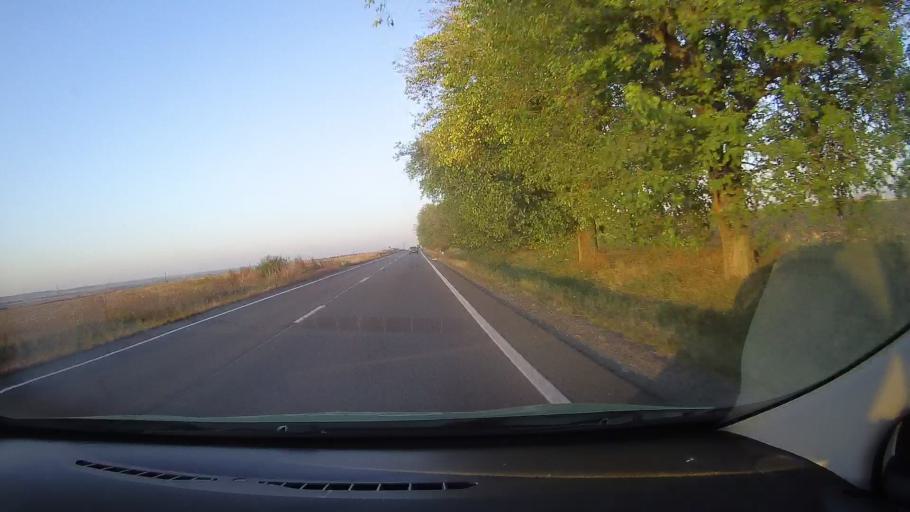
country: RO
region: Bihor
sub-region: Comuna Rosiori
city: Rosiori
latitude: 47.2679
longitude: 21.9734
